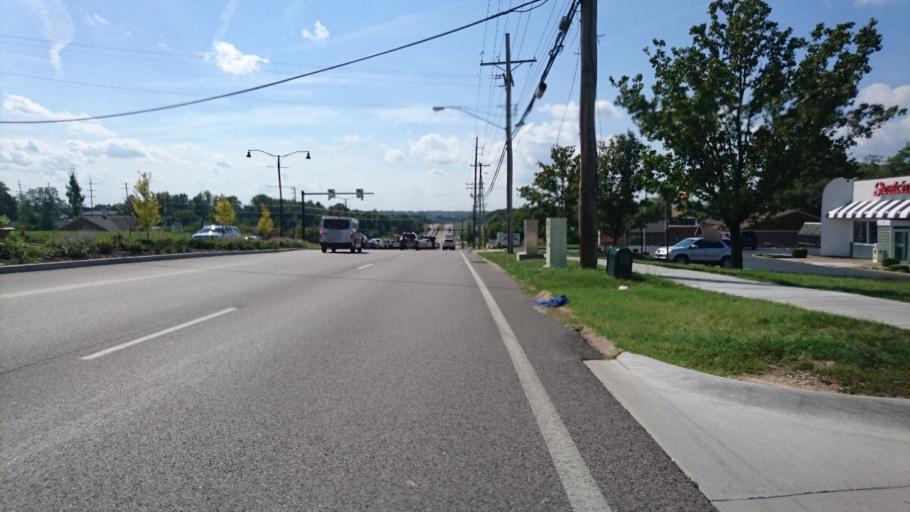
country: US
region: Missouri
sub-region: Saint Louis County
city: Ellisville
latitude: 38.5912
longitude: -90.5933
